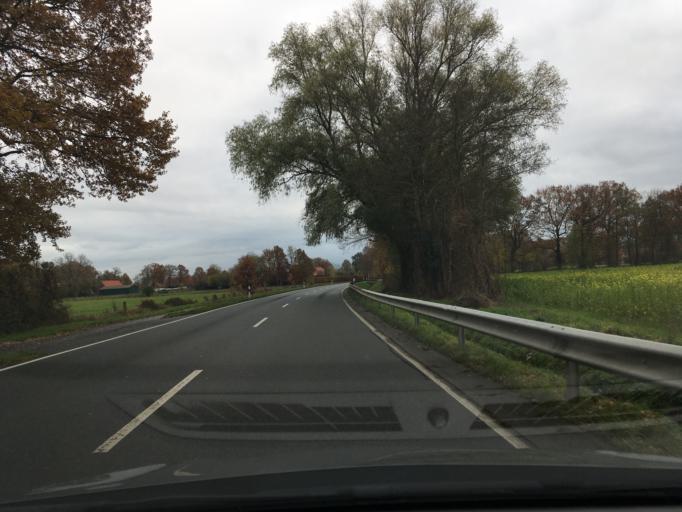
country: DE
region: North Rhine-Westphalia
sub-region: Regierungsbezirk Munster
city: Ahaus
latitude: 52.0829
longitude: 6.9713
